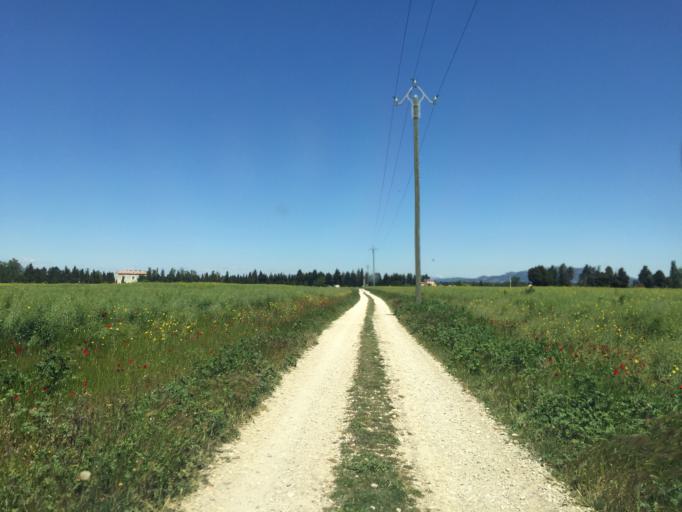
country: FR
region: Provence-Alpes-Cote d'Azur
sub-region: Departement du Vaucluse
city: Courthezon
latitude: 44.0686
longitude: 4.9038
